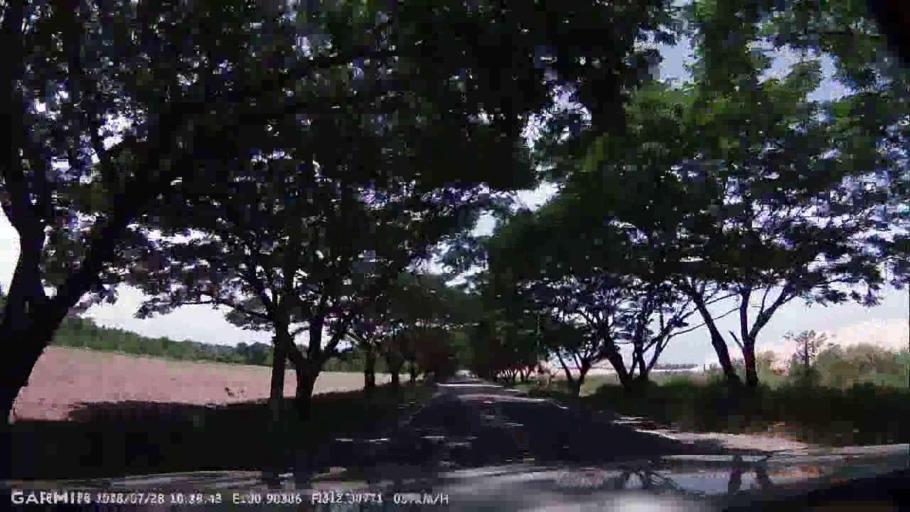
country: TH
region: Chon Buri
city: Phatthaya
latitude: 12.8977
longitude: 100.9858
